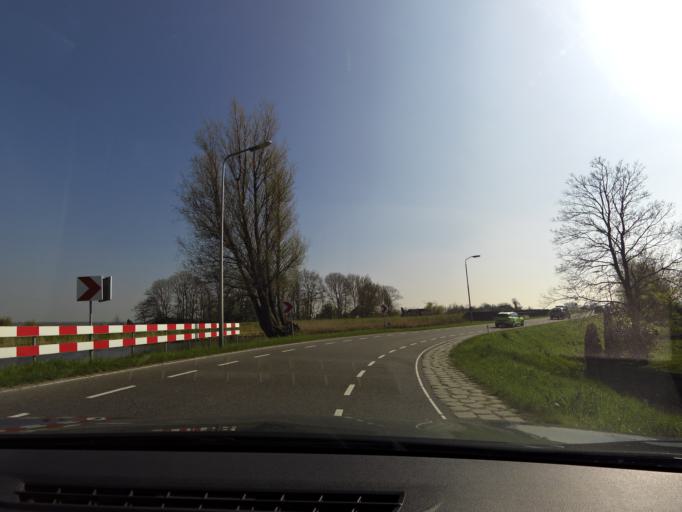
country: NL
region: South Holland
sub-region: Gemeente Westland
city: De Lier
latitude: 51.9506
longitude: 4.2781
